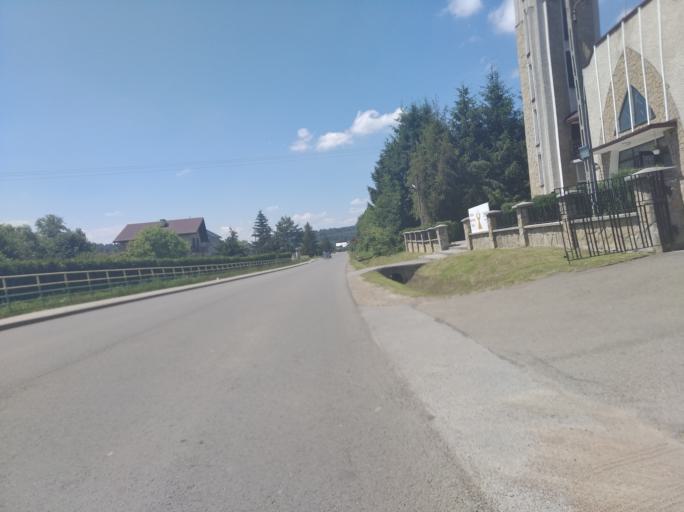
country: PL
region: Subcarpathian Voivodeship
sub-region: Powiat brzozowski
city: Niebocko
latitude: 49.6782
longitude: 22.1105
